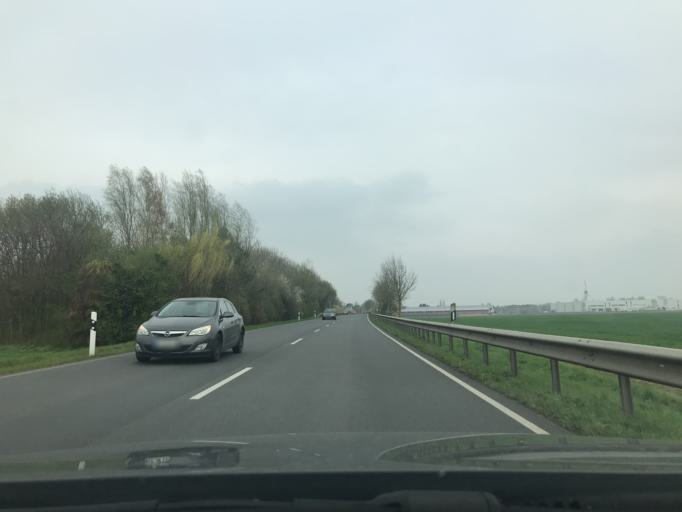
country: DE
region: North Rhine-Westphalia
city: Geldern
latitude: 51.5108
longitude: 6.2965
